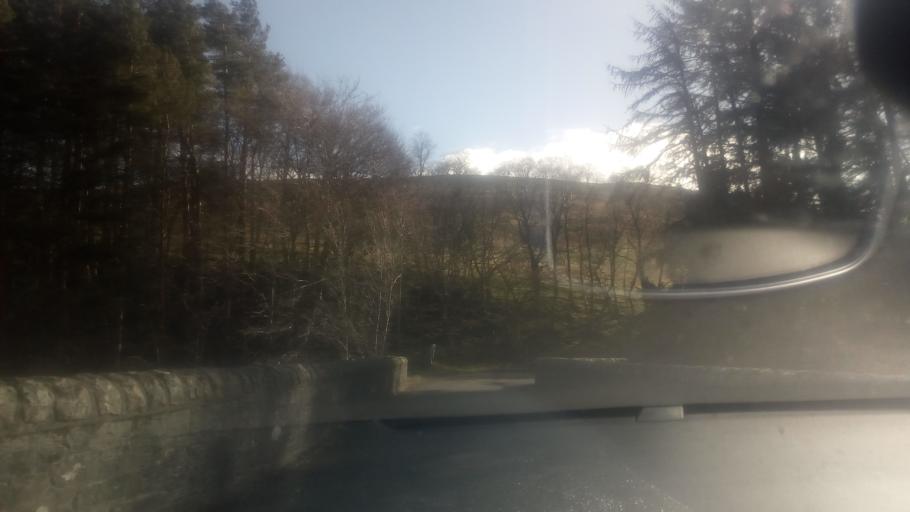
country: GB
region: Scotland
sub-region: The Scottish Borders
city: Innerleithen
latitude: 55.5114
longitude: -3.0966
